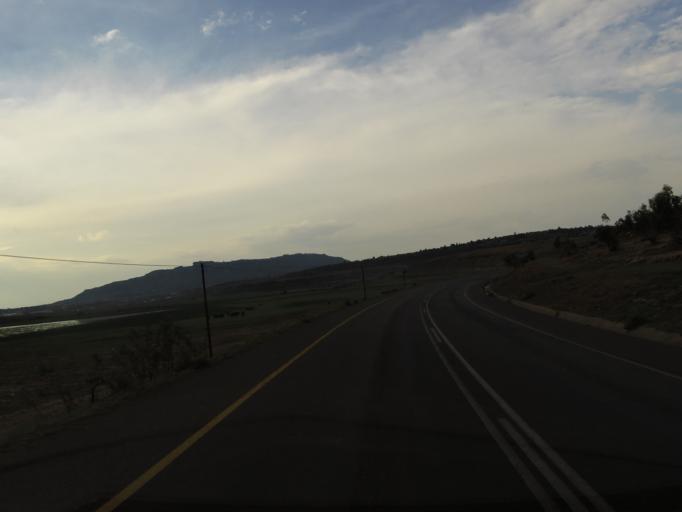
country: LS
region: Maseru
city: Maseru
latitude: -29.3920
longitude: 27.5041
